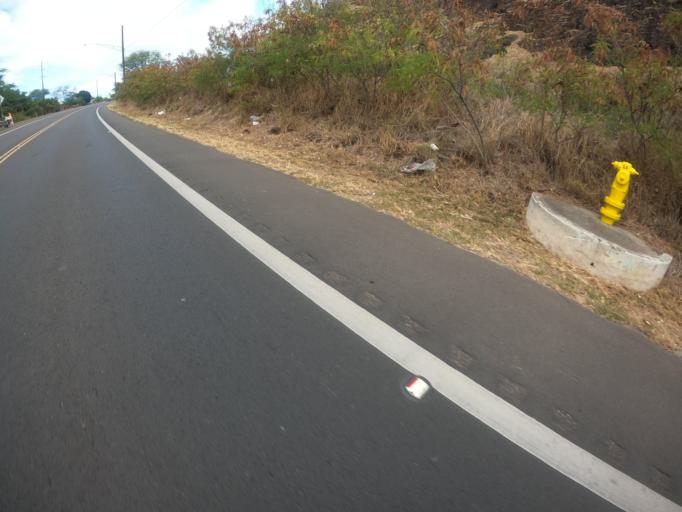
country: US
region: Hawaii
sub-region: Honolulu County
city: Makaha
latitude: 21.4807
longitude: -158.2257
